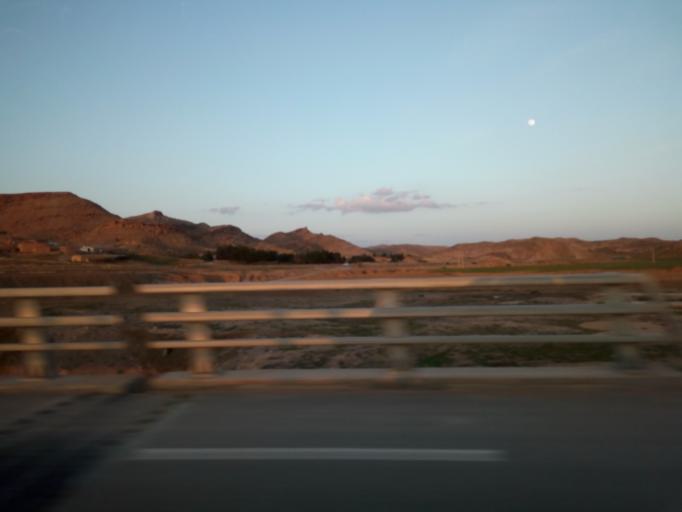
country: DZ
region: Medea
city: Ksar el Boukhari
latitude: 35.8094
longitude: 2.7665
